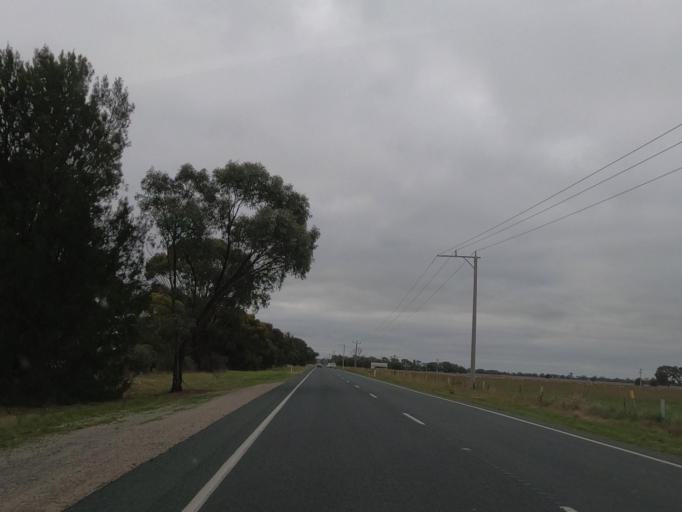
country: AU
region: Victoria
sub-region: Greater Bendigo
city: Long Gully
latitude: -36.3473
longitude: 143.9769
